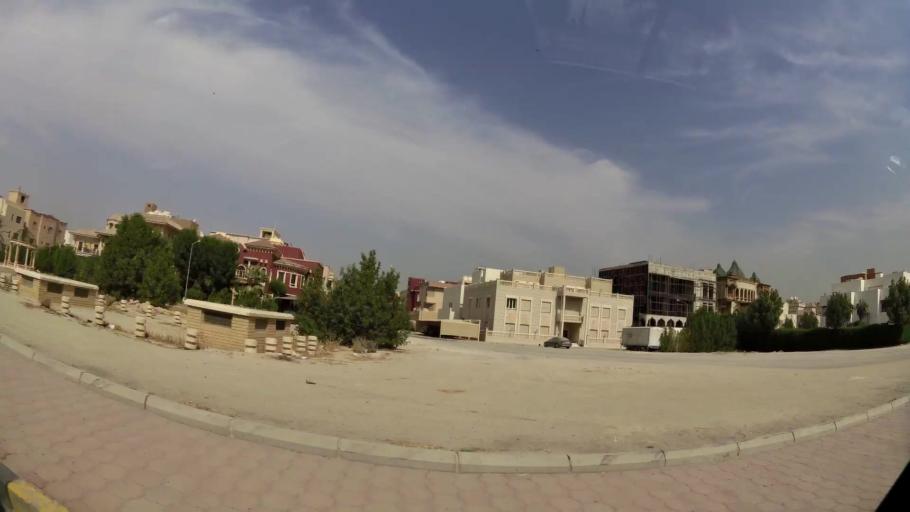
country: KW
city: Bayan
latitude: 29.2783
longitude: 48.0176
